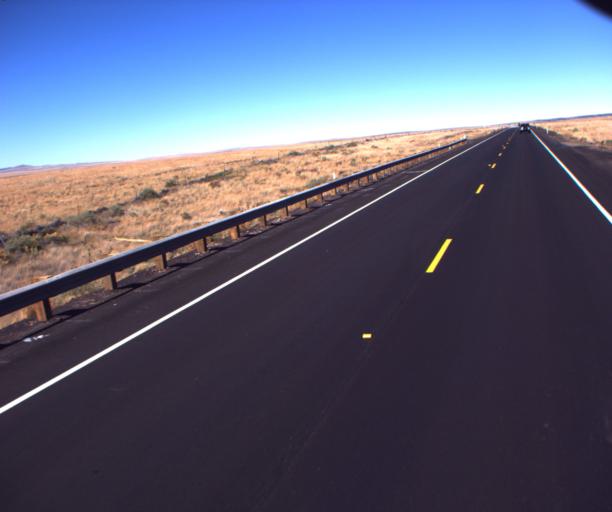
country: US
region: Arizona
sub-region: Apache County
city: Springerville
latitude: 34.2575
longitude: -109.3547
